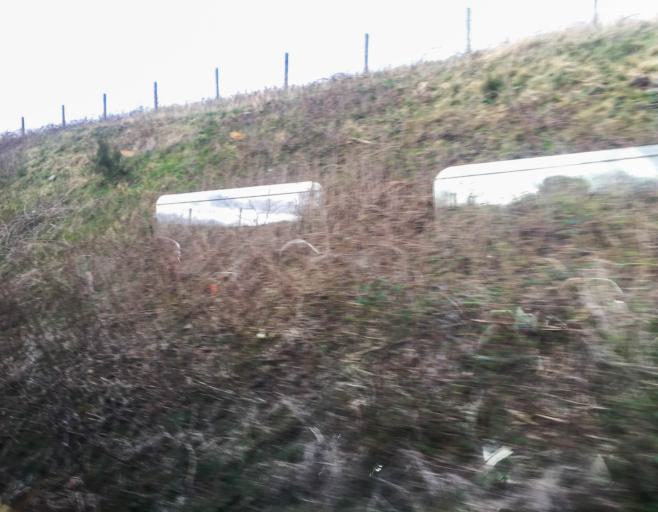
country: GB
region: Scotland
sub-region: North Lanarkshire
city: Wishaw
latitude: 55.7624
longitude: -3.9085
